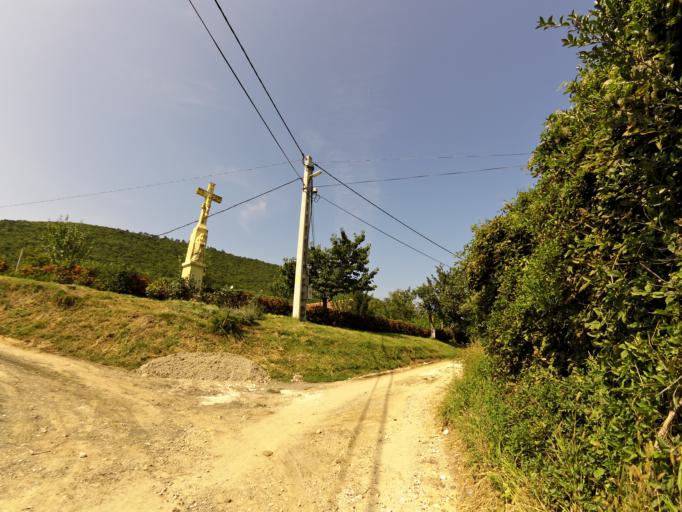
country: HU
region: Zala
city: Vonyarcvashegy
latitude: 46.8057
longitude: 17.3746
